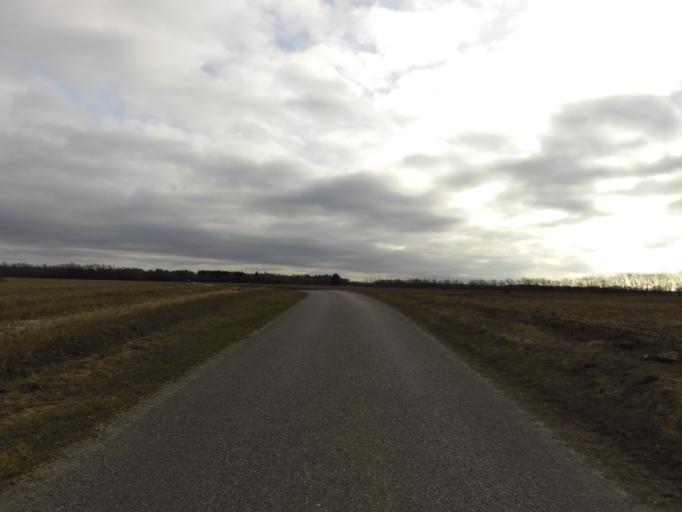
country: DK
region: South Denmark
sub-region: Tonder Kommune
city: Toftlund
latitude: 55.2047
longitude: 9.1819
